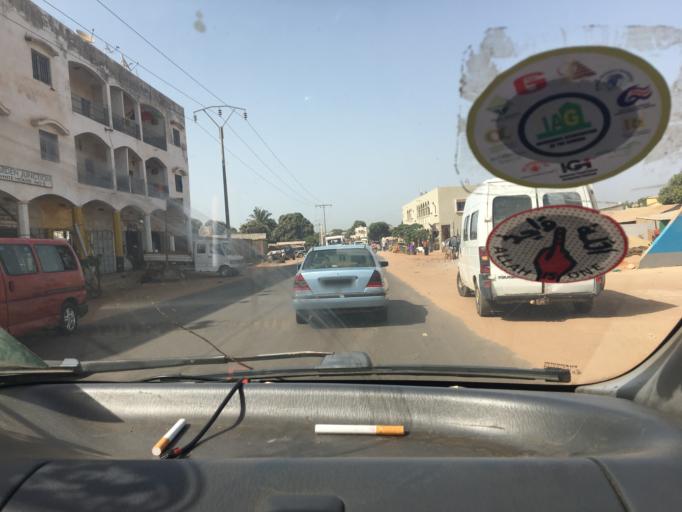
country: GM
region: Western
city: Abuko
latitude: 13.3850
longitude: -16.6780
